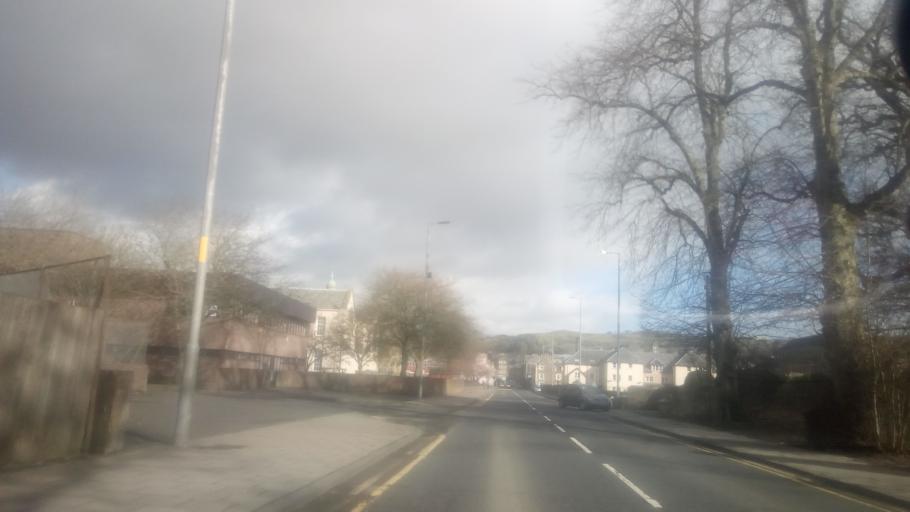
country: GB
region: Scotland
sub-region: The Scottish Borders
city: Hawick
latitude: 55.4211
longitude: -2.7966
